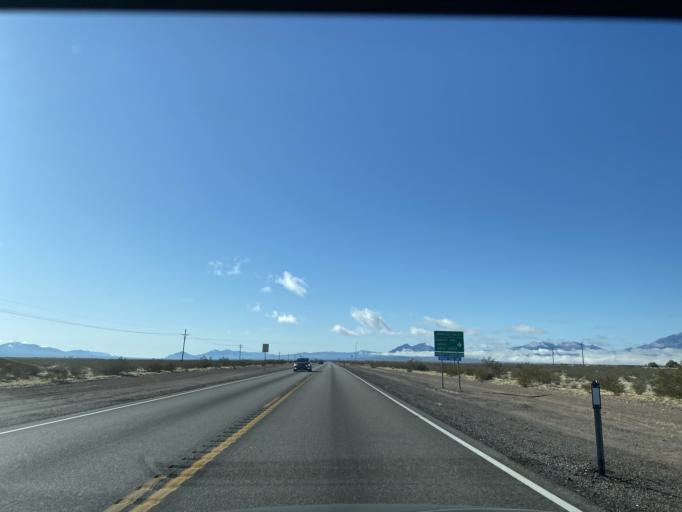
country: US
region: Nevada
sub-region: Nye County
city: Beatty
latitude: 36.5712
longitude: -116.4133
